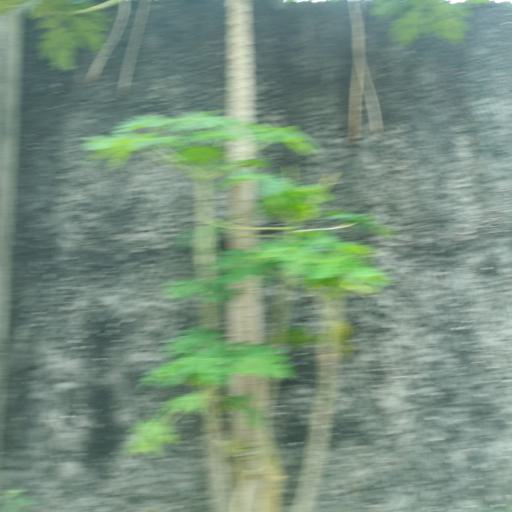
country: NG
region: Rivers
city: Port Harcourt
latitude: 4.8253
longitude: 7.0423
